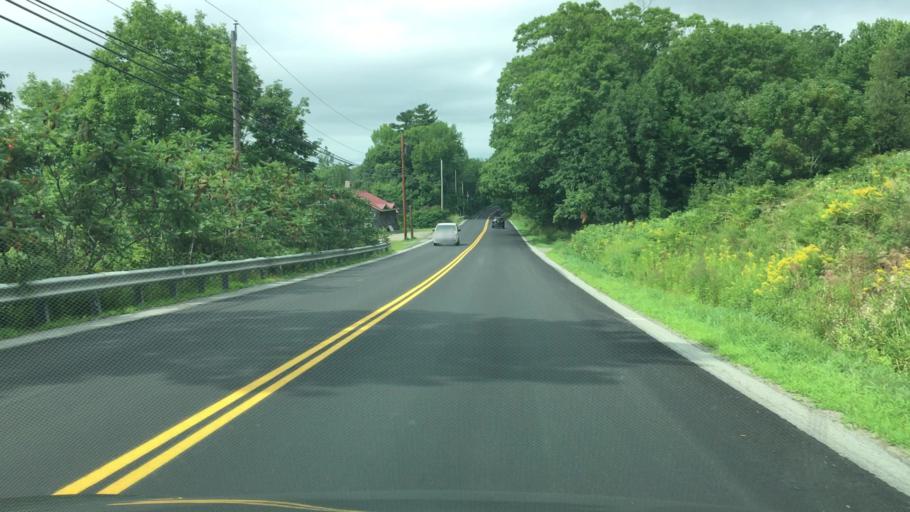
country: US
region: Maine
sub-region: Waldo County
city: Winterport
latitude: 44.6097
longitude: -68.8219
